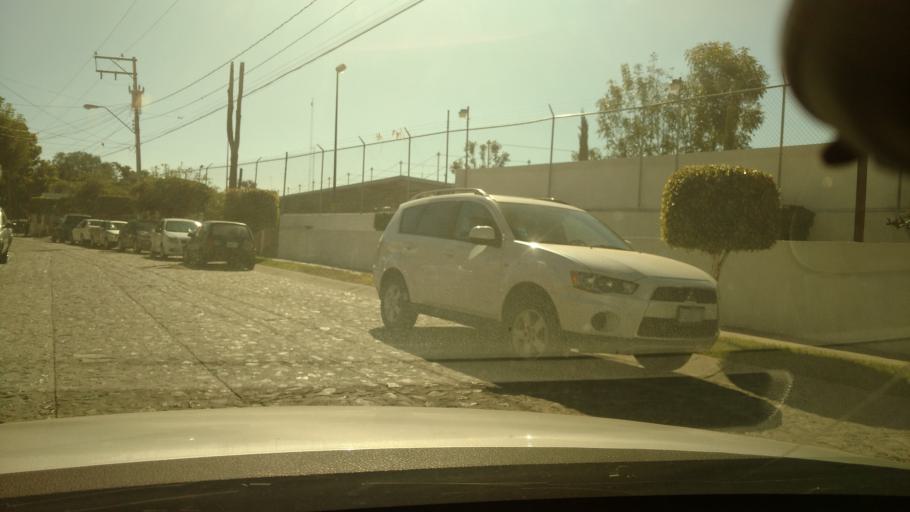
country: MX
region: Guanajuato
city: Leon
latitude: 21.1507
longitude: -101.6761
